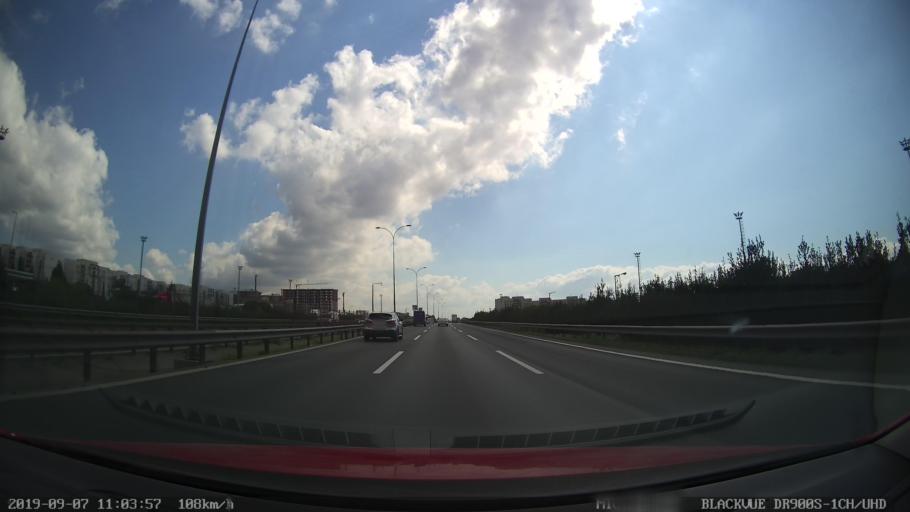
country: TR
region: Kocaeli
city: Korfez
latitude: 40.7693
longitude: 29.7934
